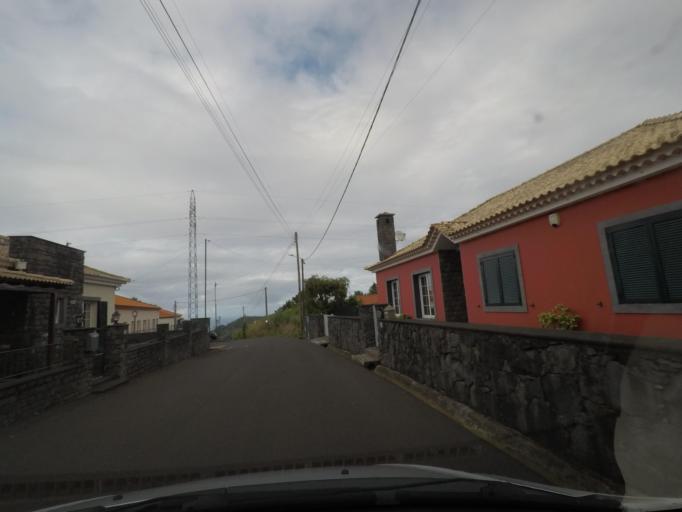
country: PT
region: Madeira
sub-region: Santana
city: Santana
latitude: 32.7907
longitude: -16.8789
